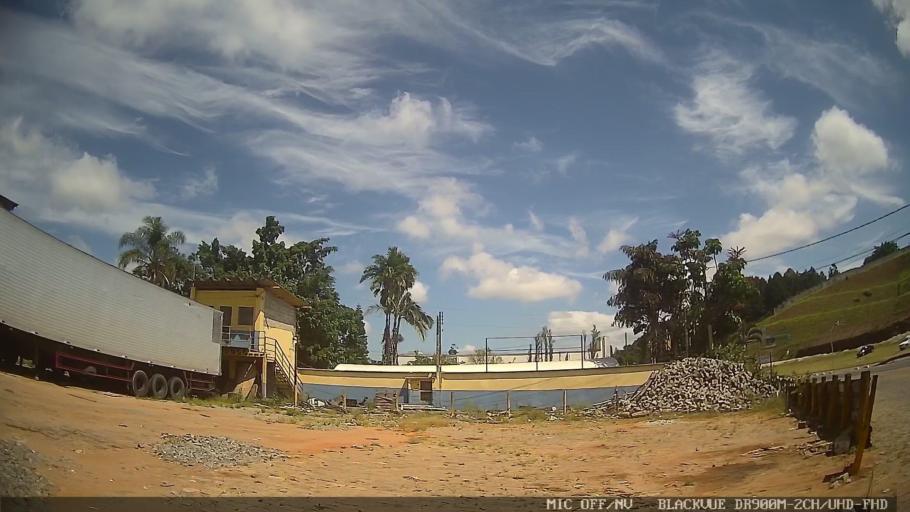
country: BR
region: Sao Paulo
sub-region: Braganca Paulista
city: Braganca Paulista
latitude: -22.9924
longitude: -46.5578
